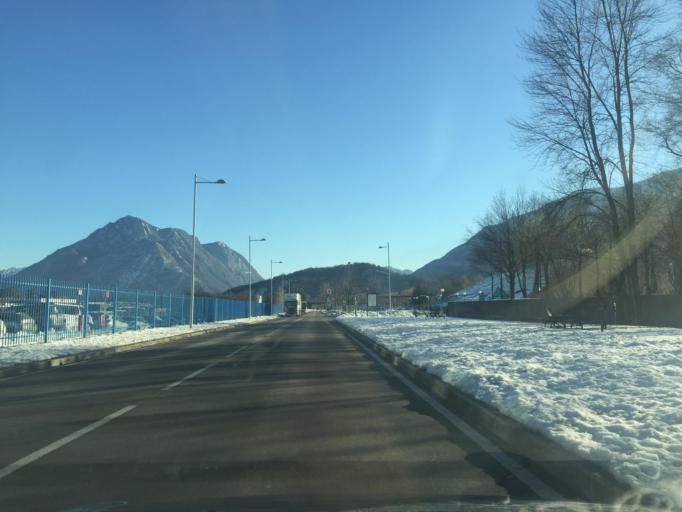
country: IT
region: Friuli Venezia Giulia
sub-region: Provincia di Udine
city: Tolmezzo
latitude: 46.3916
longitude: 13.0250
